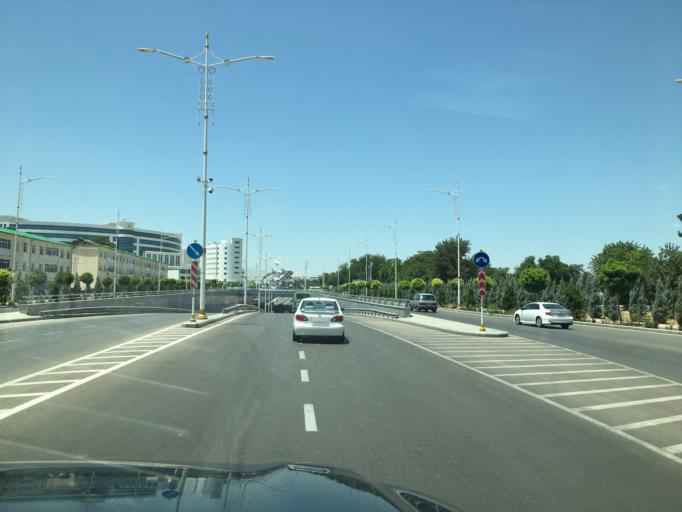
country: TM
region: Ahal
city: Ashgabat
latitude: 37.9420
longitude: 58.3684
